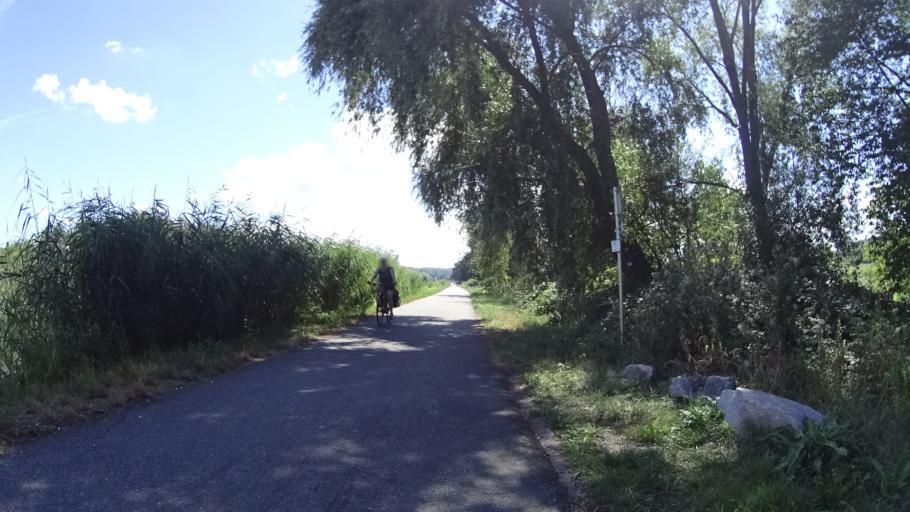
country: FR
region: Alsace
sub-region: Departement du Haut-Rhin
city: Brunstatt
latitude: 47.7177
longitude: 7.3132
